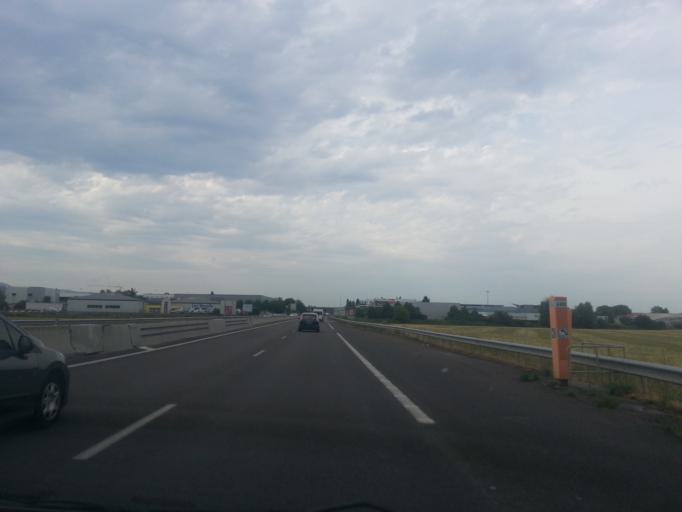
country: FR
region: Auvergne
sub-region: Departement du Puy-de-Dome
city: Perignat-les-Sarlieve
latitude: 45.7500
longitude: 3.1440
